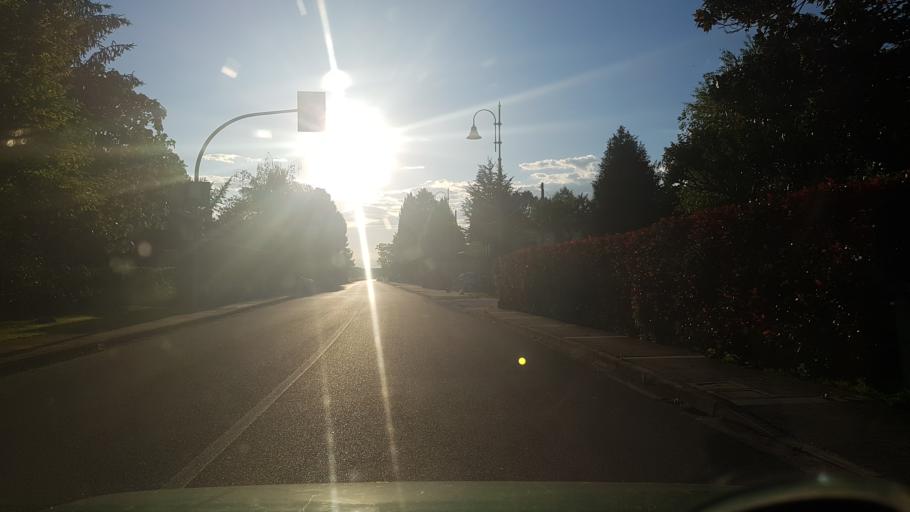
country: IT
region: Friuli Venezia Giulia
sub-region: Provincia di Udine
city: Campolongo al Torre-Cavenzano
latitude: 45.8671
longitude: 13.3913
